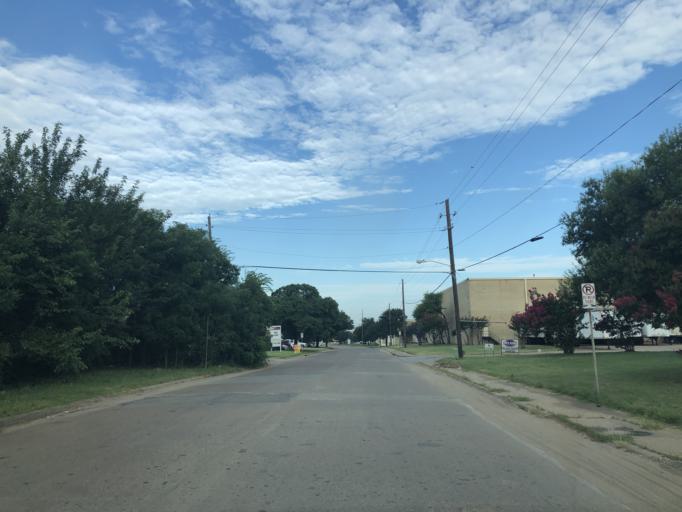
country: US
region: Texas
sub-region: Dallas County
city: Irving
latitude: 32.8105
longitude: -96.8946
